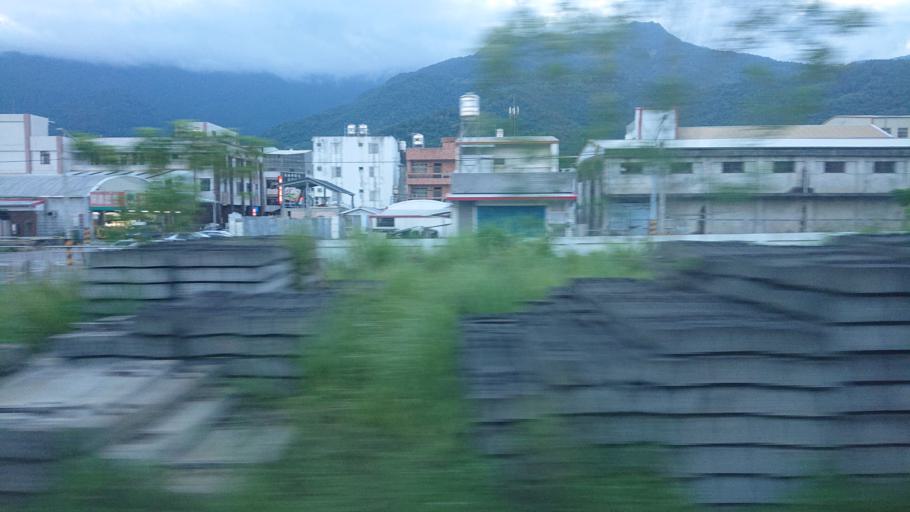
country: TW
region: Taiwan
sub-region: Taitung
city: Taitung
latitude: 23.0481
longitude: 121.1651
